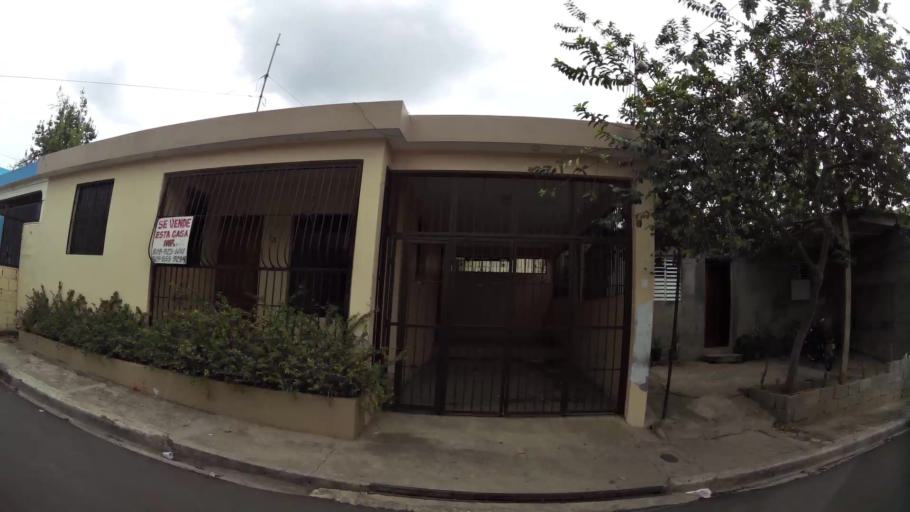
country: DO
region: Santiago
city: Santiago de los Caballeros
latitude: 19.4275
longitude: -70.6691
